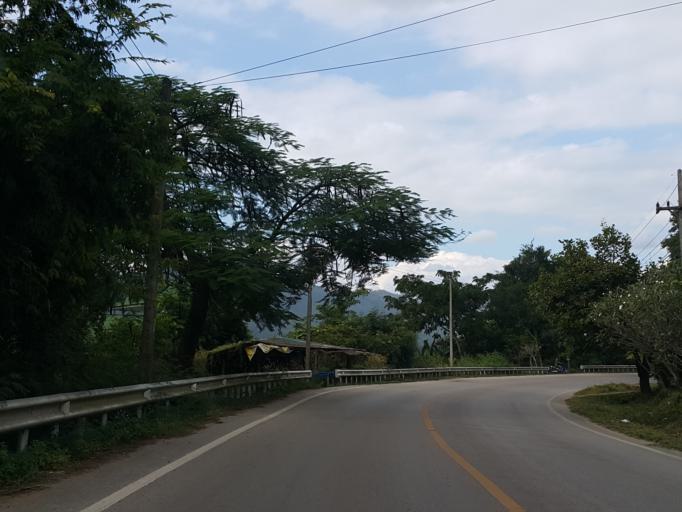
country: TH
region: Lampang
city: Chae Hom
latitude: 18.5734
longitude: 99.4691
